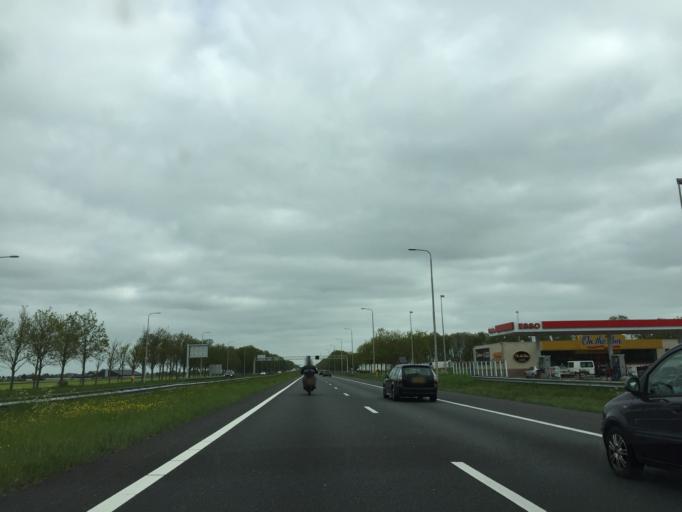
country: NL
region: North Holland
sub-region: Gemeente Beemster
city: Halfweg
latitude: 52.5460
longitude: 4.9565
